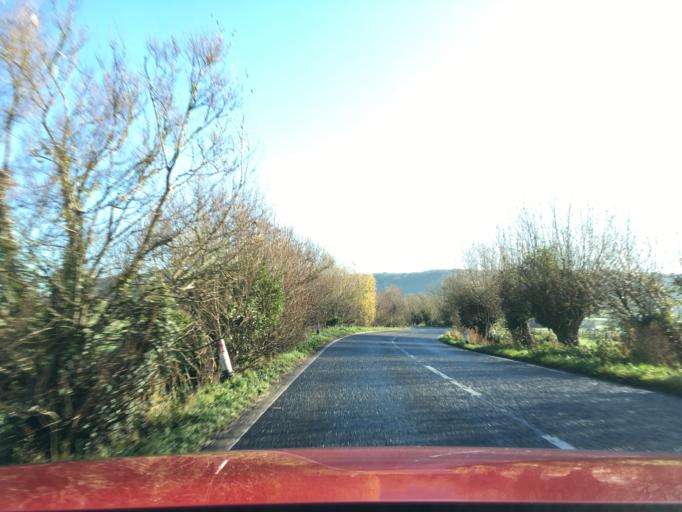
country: GB
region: England
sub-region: Somerset
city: Langport
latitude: 51.0786
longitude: -2.8623
